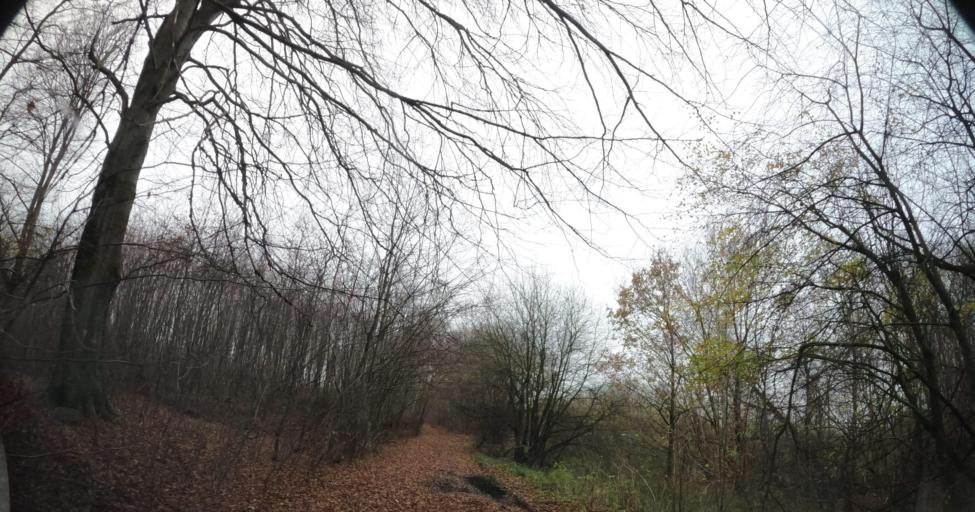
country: PL
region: West Pomeranian Voivodeship
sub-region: Powiat drawski
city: Drawsko Pomorskie
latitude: 53.5971
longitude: 15.7752
